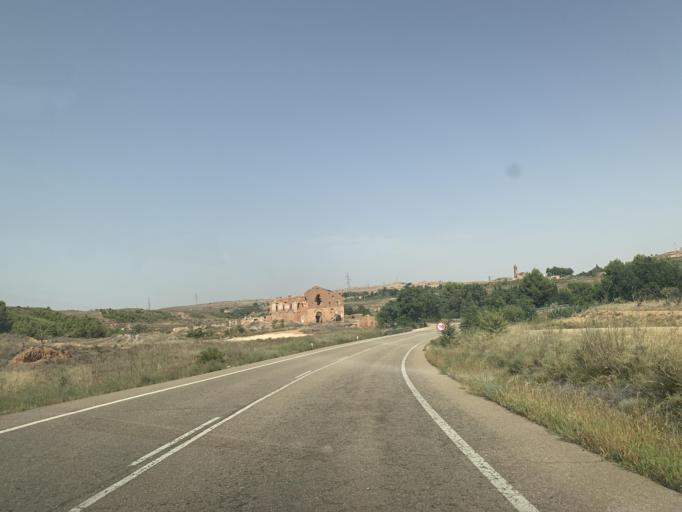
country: ES
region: Aragon
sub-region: Provincia de Zaragoza
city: Belchite
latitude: 41.2915
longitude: -0.7362
